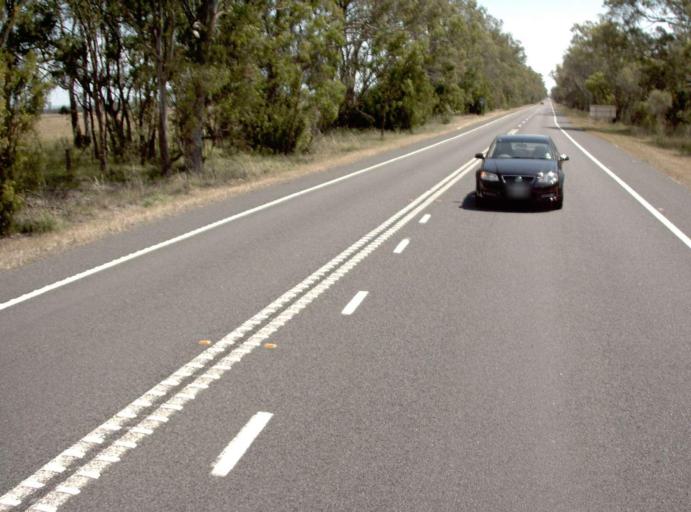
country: AU
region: Victoria
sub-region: Wellington
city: Sale
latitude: -37.9473
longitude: 147.1196
